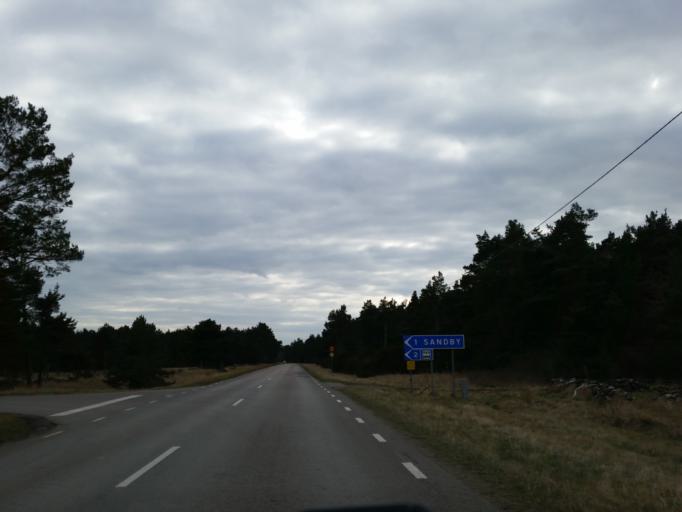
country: SE
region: Kalmar
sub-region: Morbylanga Kommun
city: Sodra Sandby
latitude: 56.5848
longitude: 16.6245
